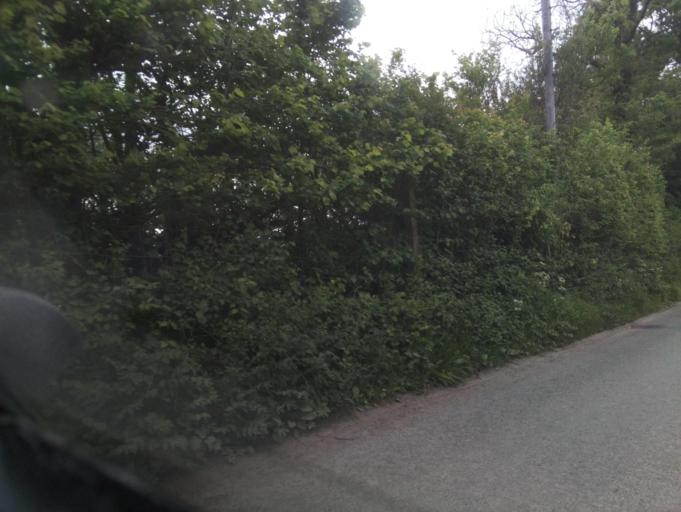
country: GB
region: England
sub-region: Herefordshire
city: Ledbury
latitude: 52.0352
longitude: -2.4489
